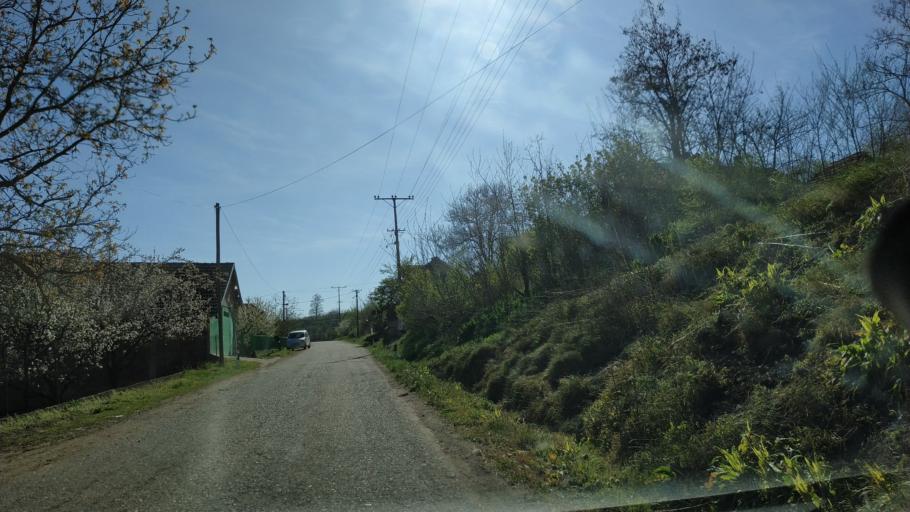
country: RS
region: Central Serbia
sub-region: Nisavski Okrug
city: Aleksinac
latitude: 43.4851
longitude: 21.6580
